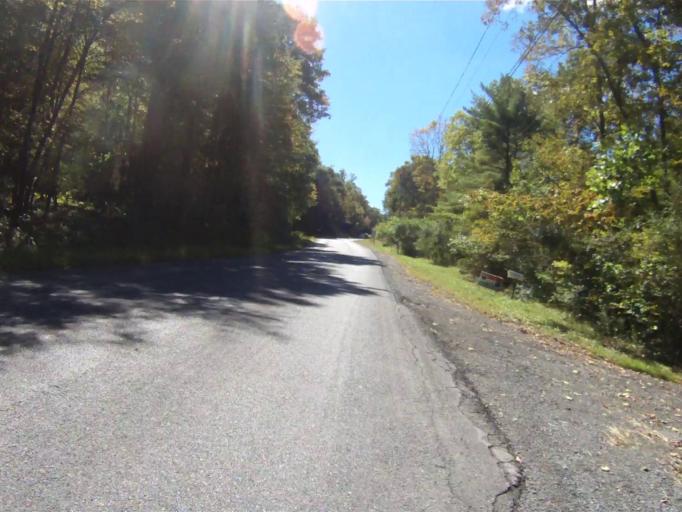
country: US
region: Pennsylvania
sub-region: Centre County
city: Houserville
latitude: 40.8958
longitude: -77.8774
